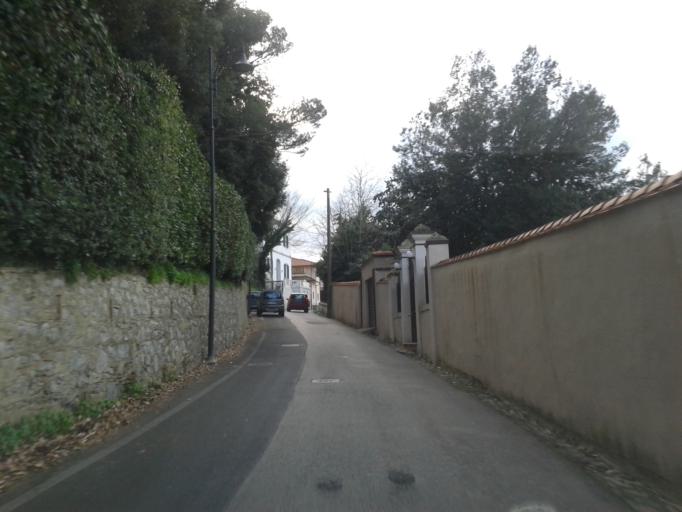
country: IT
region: Tuscany
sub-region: Provincia di Livorno
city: Quercianella
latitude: 43.4951
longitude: 10.3518
